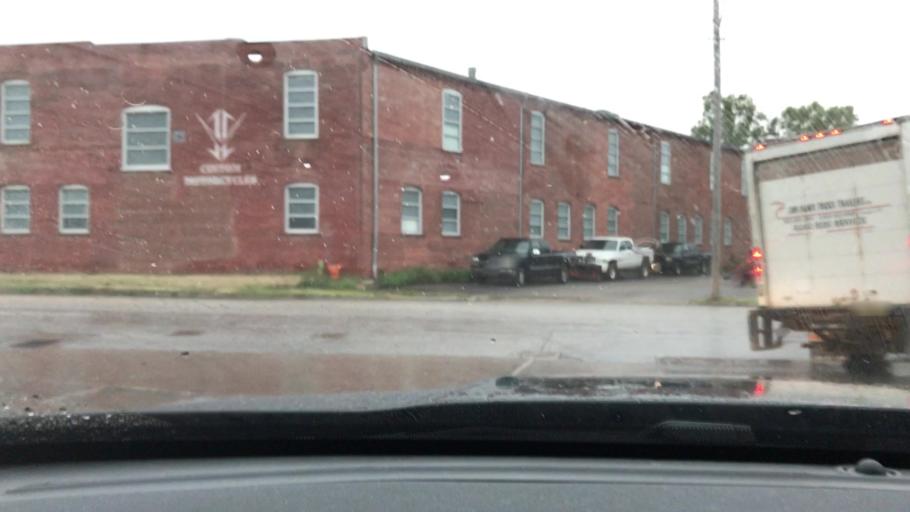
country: US
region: Iowa
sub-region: Scott County
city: Davenport
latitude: 41.5192
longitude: -90.6016
